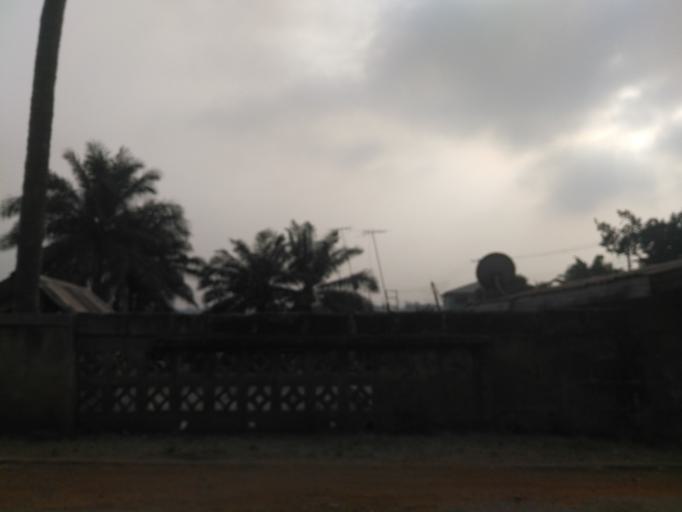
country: GH
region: Ashanti
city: Kumasi
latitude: 6.6912
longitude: -1.6013
